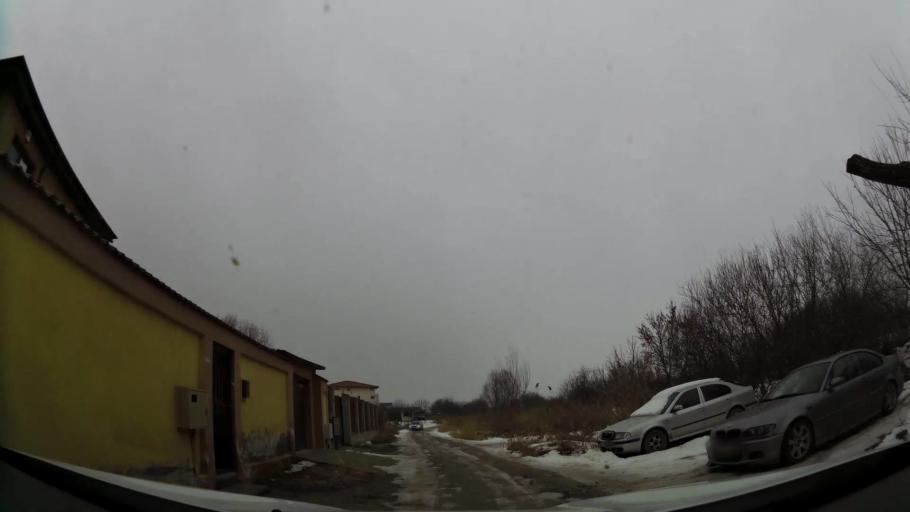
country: RO
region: Ilfov
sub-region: Comuna Popesti-Leordeni
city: Popesti-Leordeni
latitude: 44.4017
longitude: 26.1690
